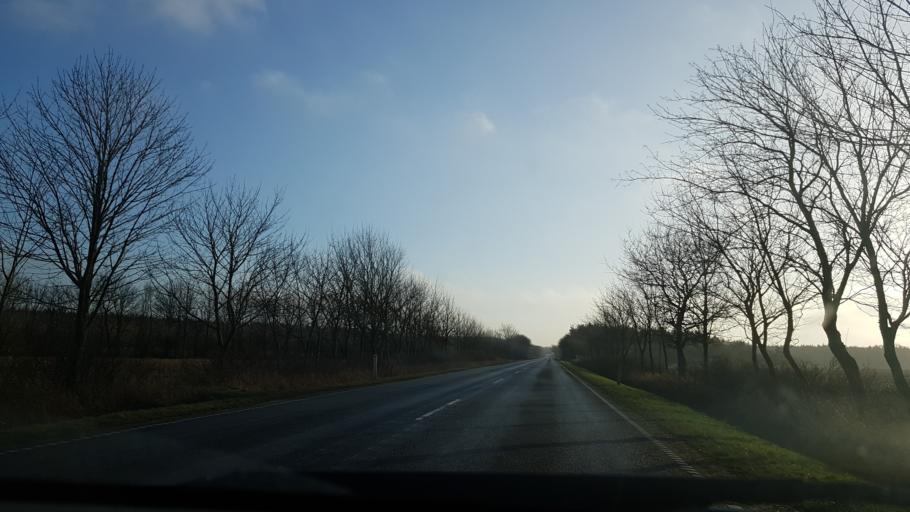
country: DK
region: South Denmark
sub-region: Tonder Kommune
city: Toftlund
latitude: 55.2096
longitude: 9.1886
